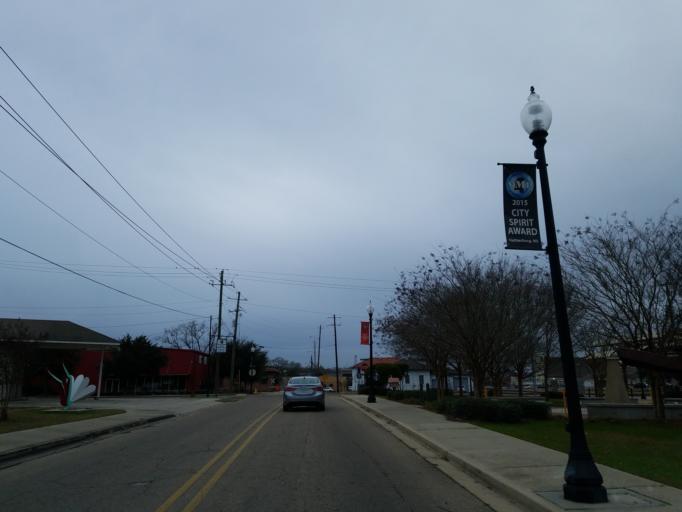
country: US
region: Mississippi
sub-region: Forrest County
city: Hattiesburg
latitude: 31.3265
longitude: -89.2868
